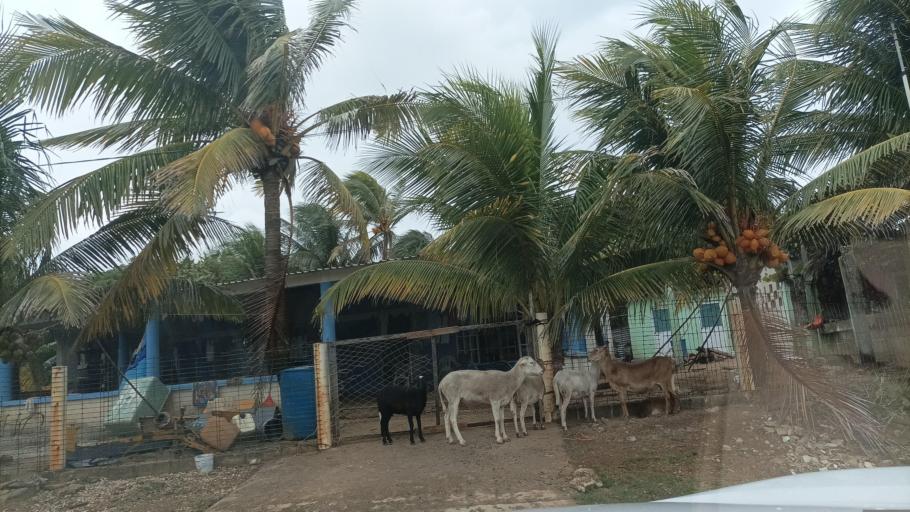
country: MX
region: Veracruz
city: Agua Dulce
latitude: 18.2108
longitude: -94.1395
